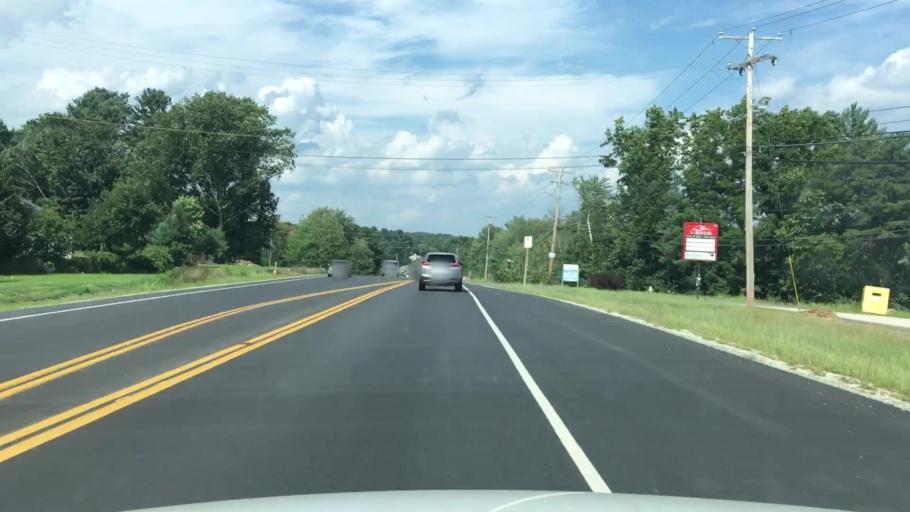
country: US
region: New Hampshire
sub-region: Rockingham County
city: Londonderry
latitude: 42.8507
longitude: -71.3578
